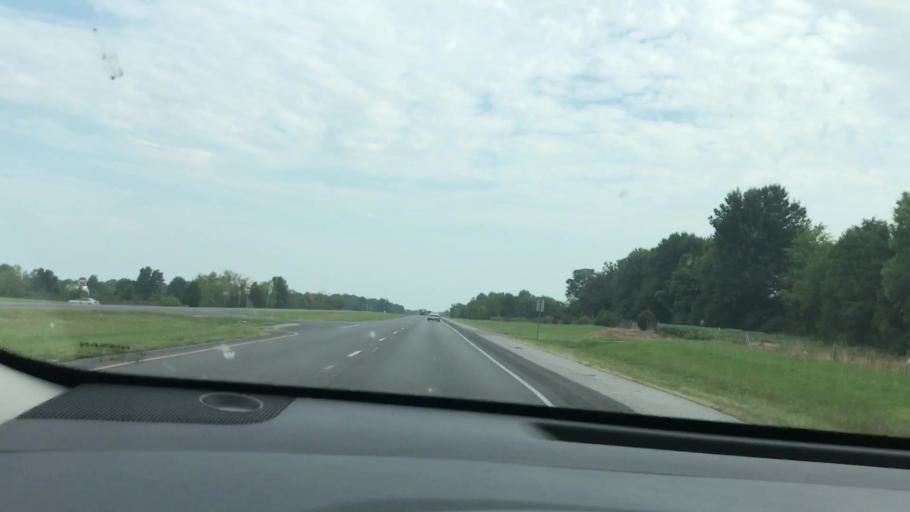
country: US
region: Kentucky
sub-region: Calloway County
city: Murray
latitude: 36.6910
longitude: -88.3030
